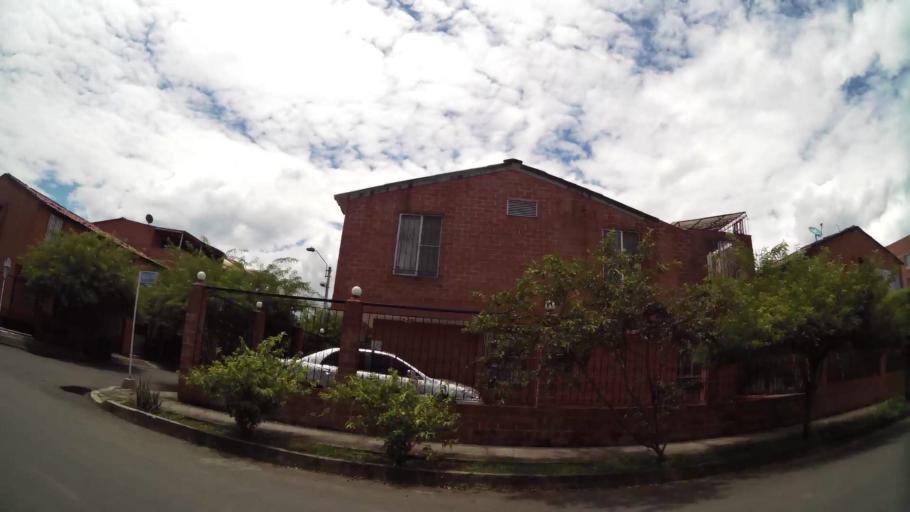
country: CO
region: Valle del Cauca
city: Cali
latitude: 3.3779
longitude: -76.5143
